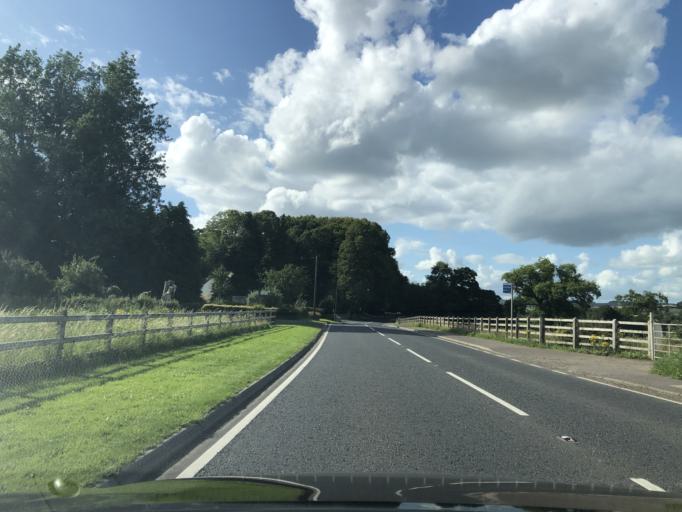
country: GB
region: Northern Ireland
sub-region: Ards District
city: Comber
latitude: 54.5622
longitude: -5.7640
